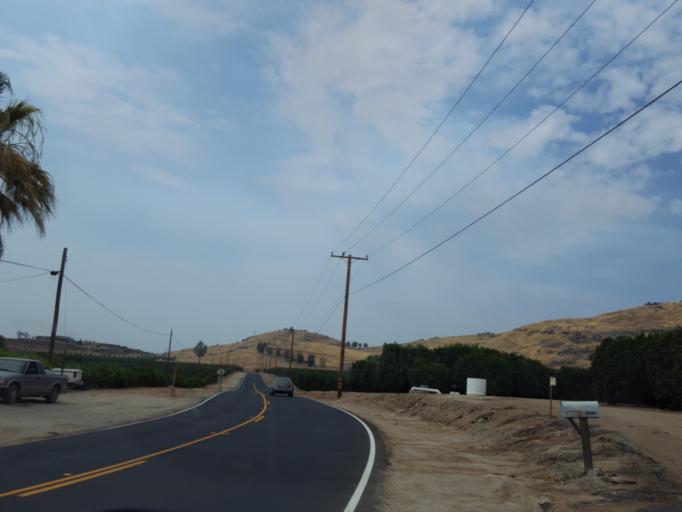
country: US
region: California
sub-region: Tulare County
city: Woodlake
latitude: 36.4064
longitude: -119.0409
